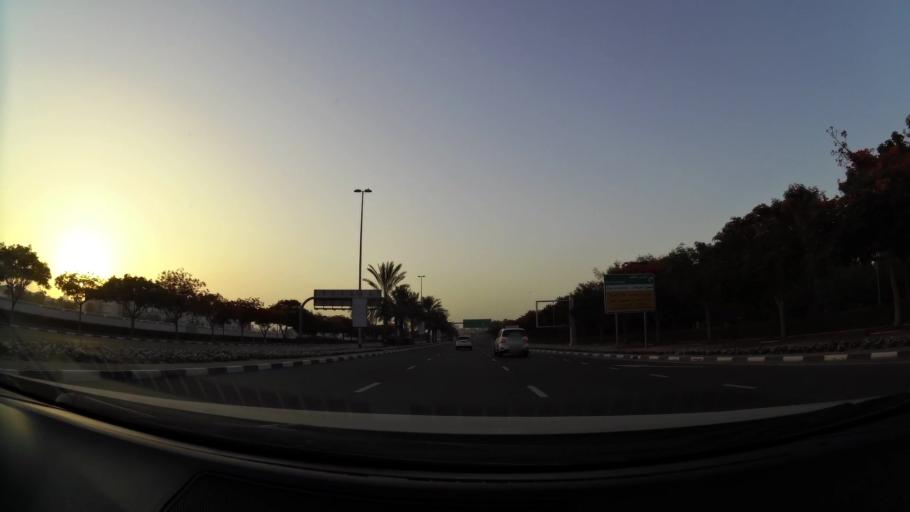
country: AE
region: Ash Shariqah
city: Sharjah
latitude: 25.2418
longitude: 55.3233
